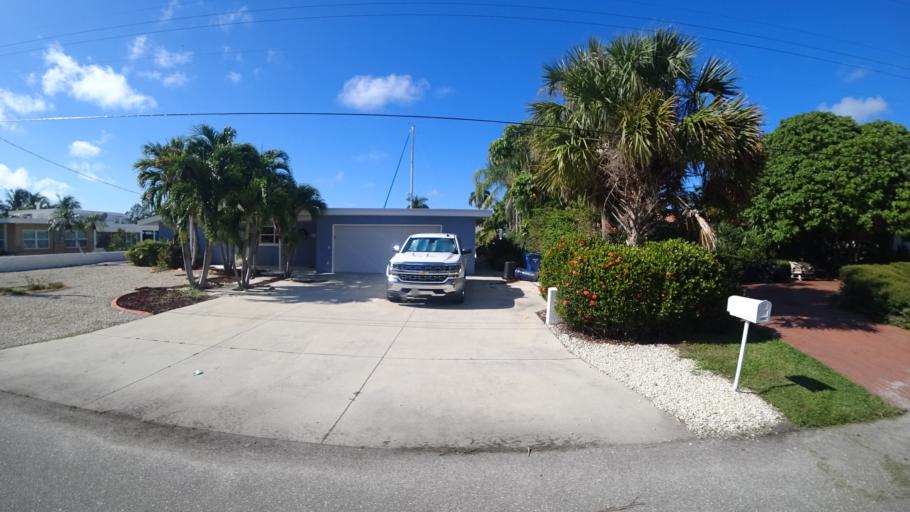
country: US
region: Florida
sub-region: Manatee County
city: Anna Maria
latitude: 27.5220
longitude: -82.7209
